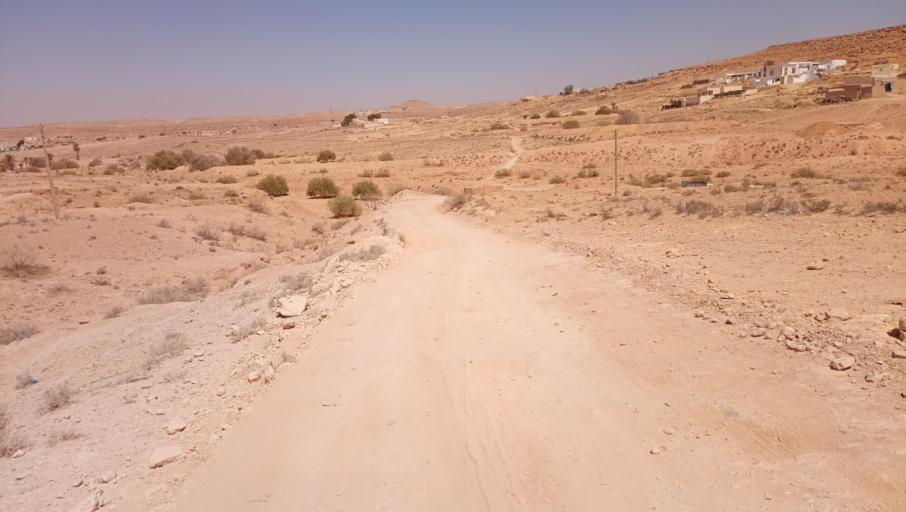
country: TN
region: Tataouine
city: Tataouine
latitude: 32.7833
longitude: 10.5138
